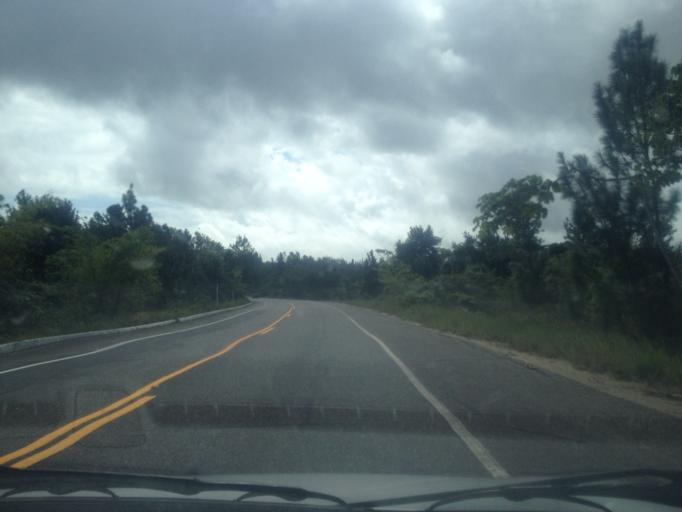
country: BR
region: Bahia
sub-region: Entre Rios
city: Entre Rios
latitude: -12.1412
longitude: -37.7918
